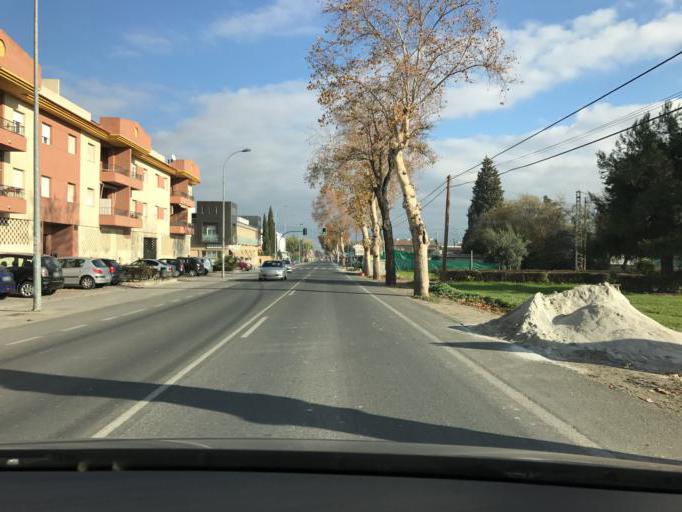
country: ES
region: Andalusia
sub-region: Provincia de Granada
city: Alhendin
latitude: 37.1078
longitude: -3.6412
